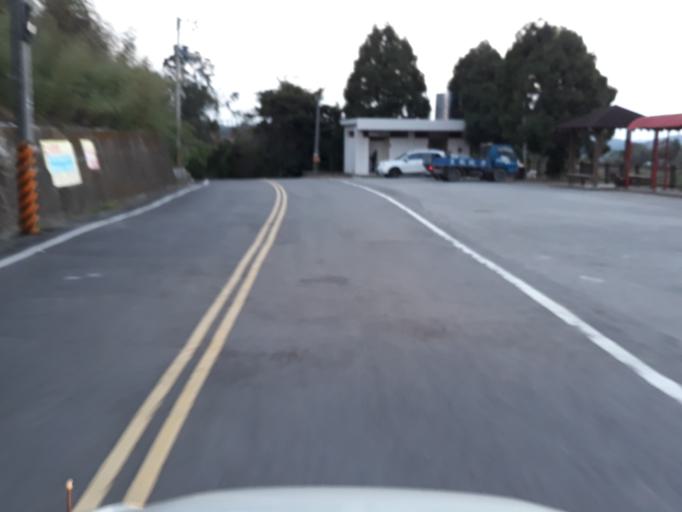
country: TW
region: Taiwan
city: Fengyuan
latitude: 24.3587
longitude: 120.8681
